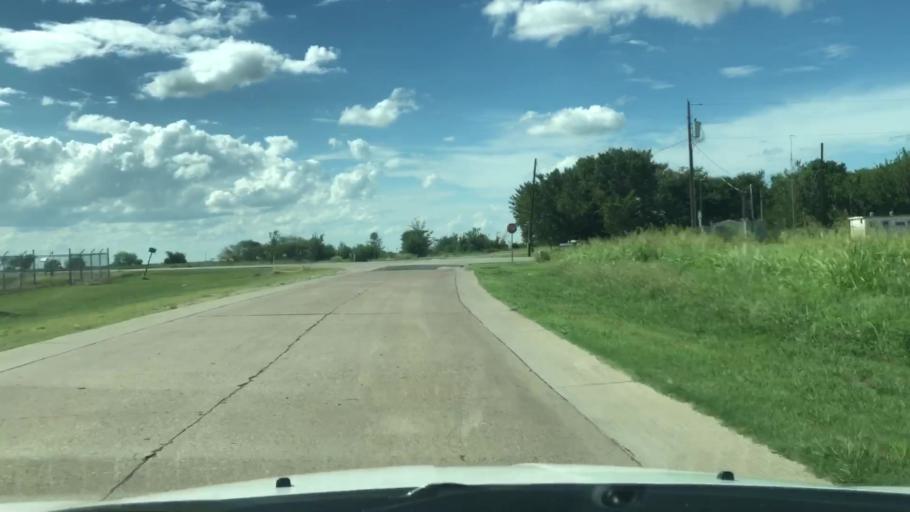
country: US
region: Texas
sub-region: Navarro County
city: Corsicana
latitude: 32.0347
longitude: -96.4023
